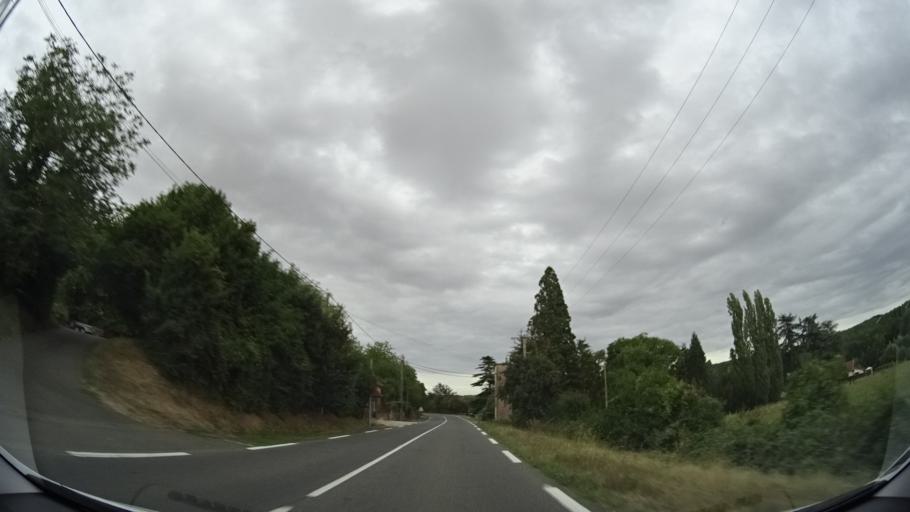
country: FR
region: Centre
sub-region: Departement du Loiret
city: Saint-Germain-des-Pres
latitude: 47.9339
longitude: 2.9024
